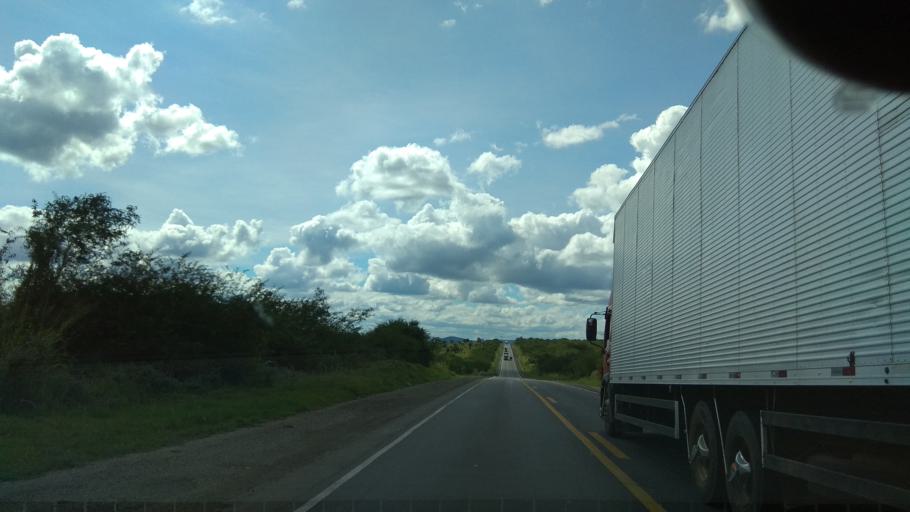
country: BR
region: Bahia
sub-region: Jaguaquara
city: Jaguaquara
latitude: -13.4417
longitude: -40.0302
